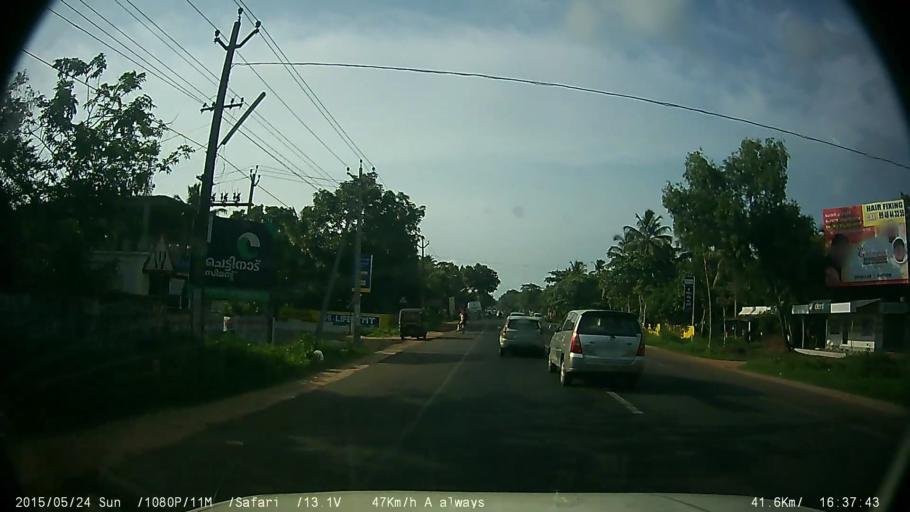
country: IN
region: Kerala
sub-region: Alappuzha
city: Shertallai
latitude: 9.6056
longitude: 76.3290
